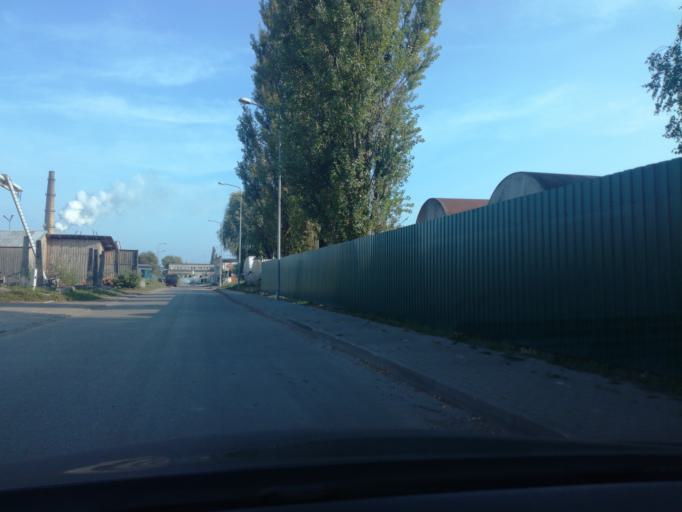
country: LT
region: Alytaus apskritis
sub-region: Alytus
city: Alytus
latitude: 54.4339
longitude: 24.0239
